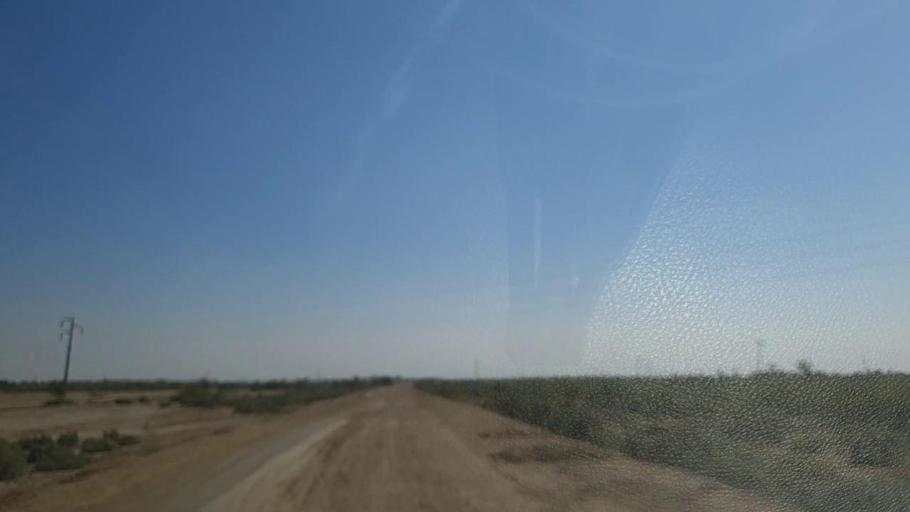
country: PK
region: Sindh
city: Samaro
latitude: 25.3045
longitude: 69.4805
